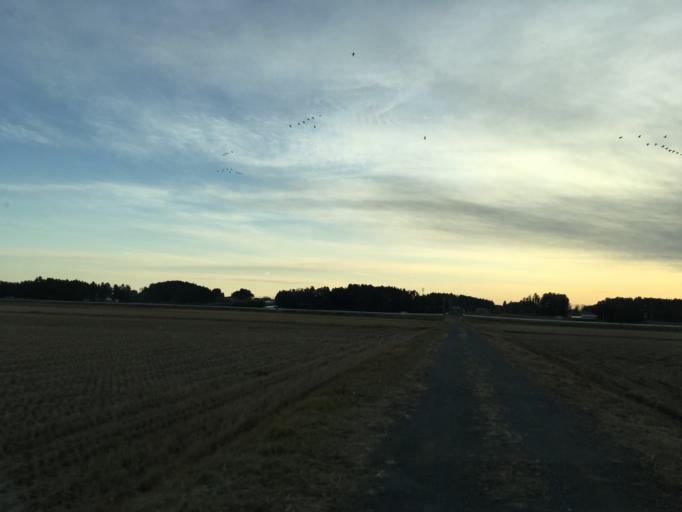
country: JP
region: Miyagi
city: Kogota
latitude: 38.6454
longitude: 141.0631
